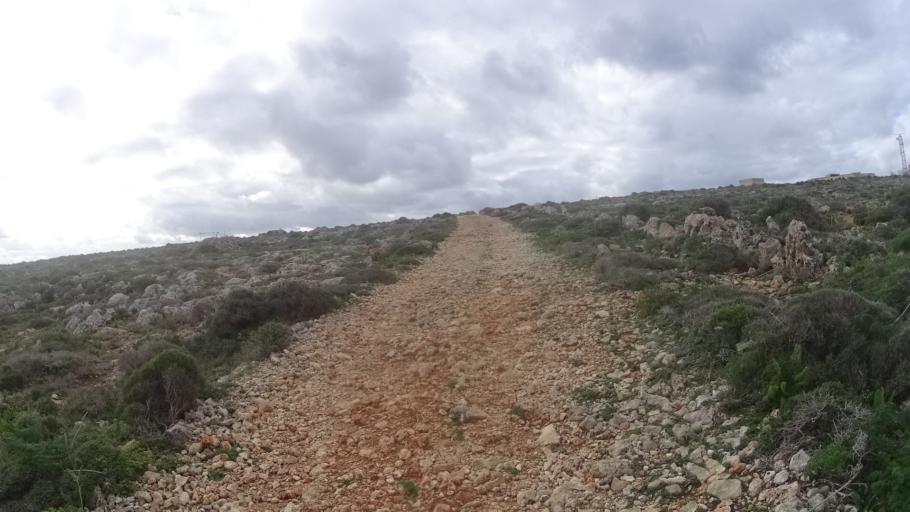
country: MT
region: Il-Mellieha
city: Mellieha
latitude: 35.9736
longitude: 14.3264
